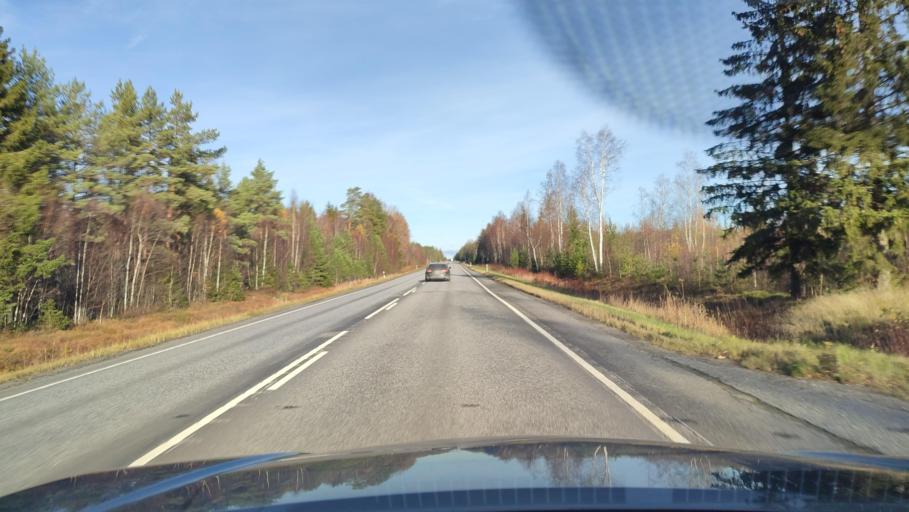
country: FI
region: Ostrobothnia
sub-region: Vaasa
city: Malax
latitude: 62.7873
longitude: 21.6683
